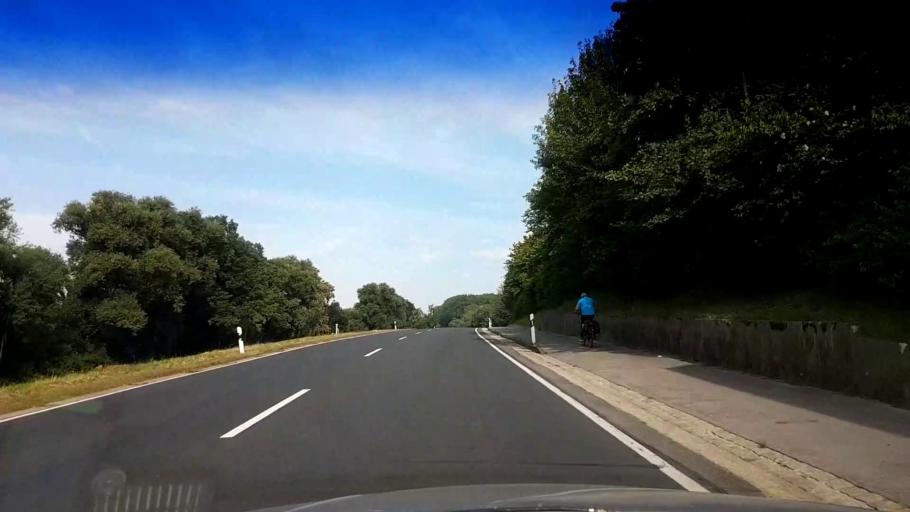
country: DE
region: Bavaria
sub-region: Regierungsbezirk Unterfranken
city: Eltmann
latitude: 49.9698
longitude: 10.6778
